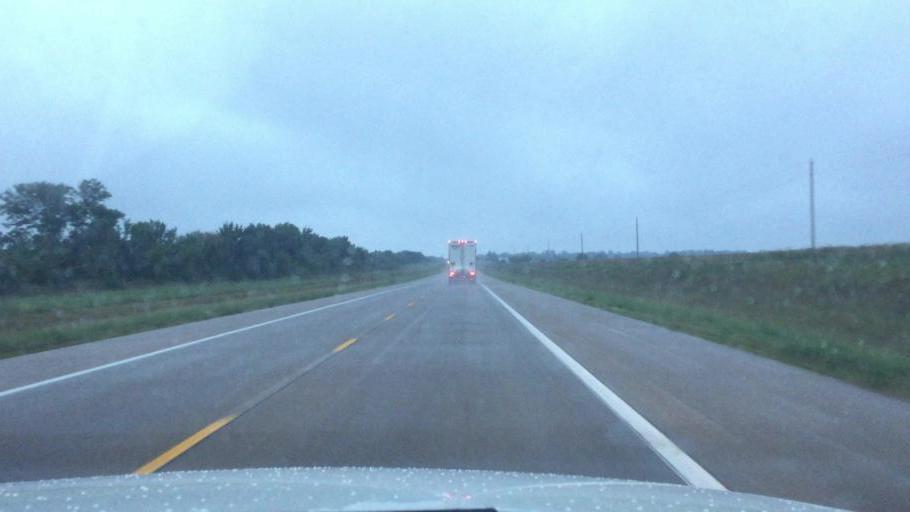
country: US
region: Kansas
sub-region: Neosho County
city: Chanute
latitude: 37.5122
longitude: -95.4709
